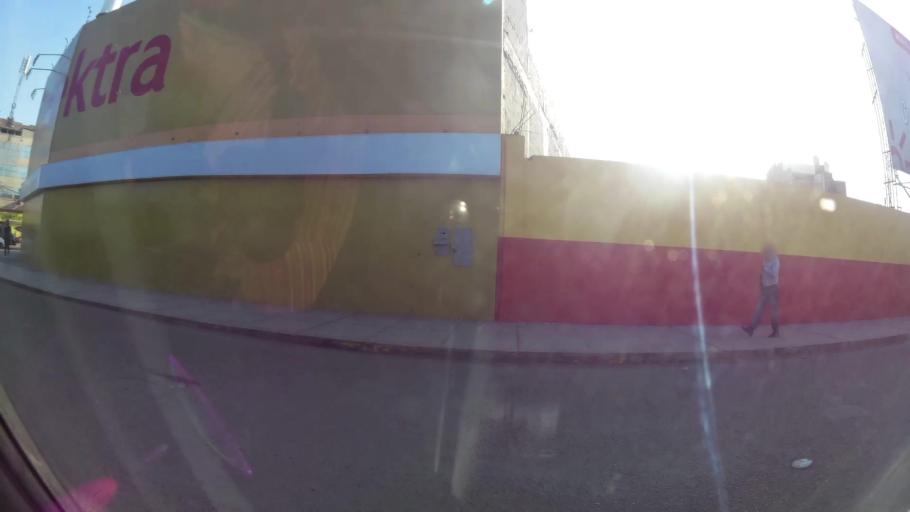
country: PE
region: Lambayeque
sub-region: Provincia de Chiclayo
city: Chiclayo
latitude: -6.7708
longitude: -79.8452
